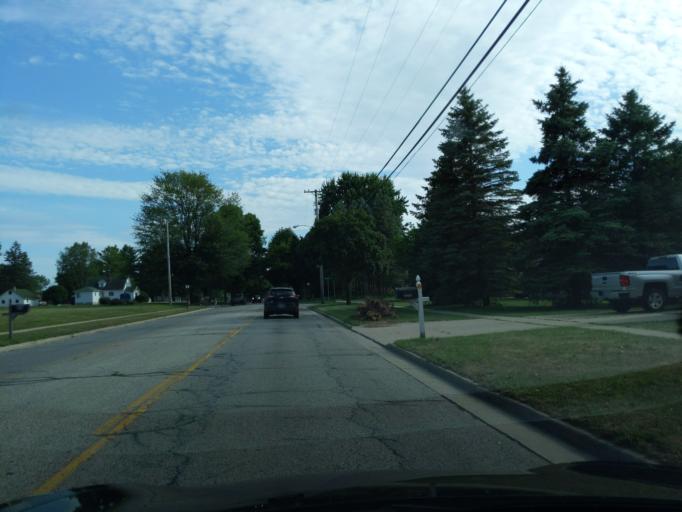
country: US
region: Michigan
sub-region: Midland County
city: Midland
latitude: 43.6515
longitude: -84.2270
